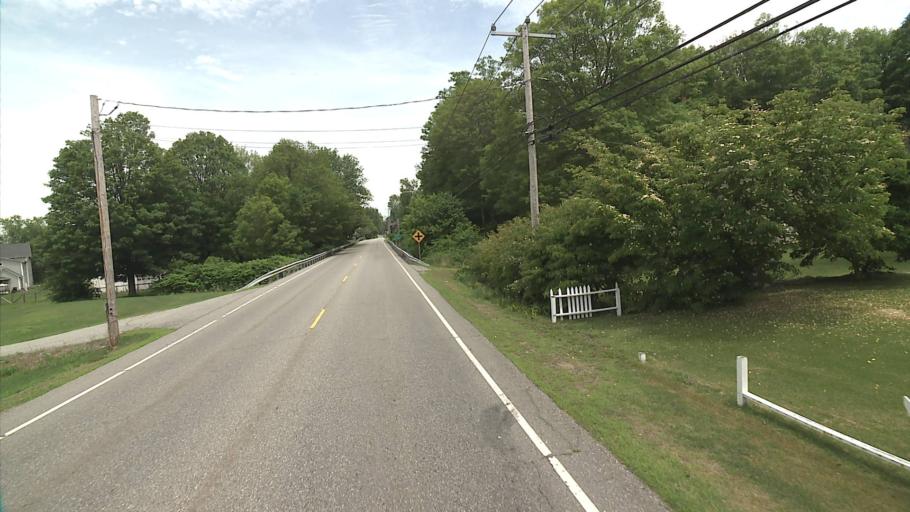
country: US
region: Connecticut
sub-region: New London County
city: Preston City
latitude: 41.5269
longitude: -71.9765
